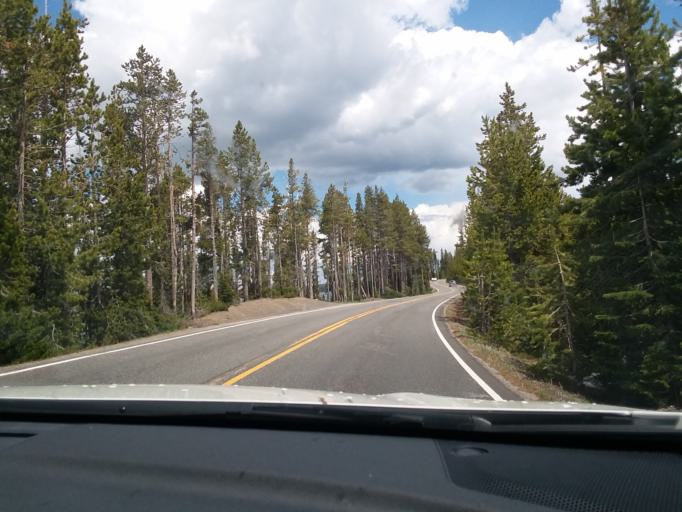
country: US
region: Montana
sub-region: Gallatin County
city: West Yellowstone
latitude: 44.2871
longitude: -110.6265
